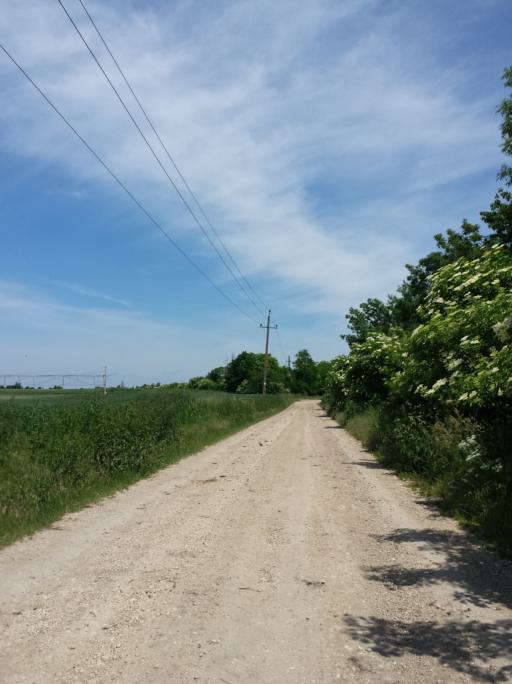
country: CZ
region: South Moravian
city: Jaroslavice
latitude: 48.7301
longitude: 16.2667
